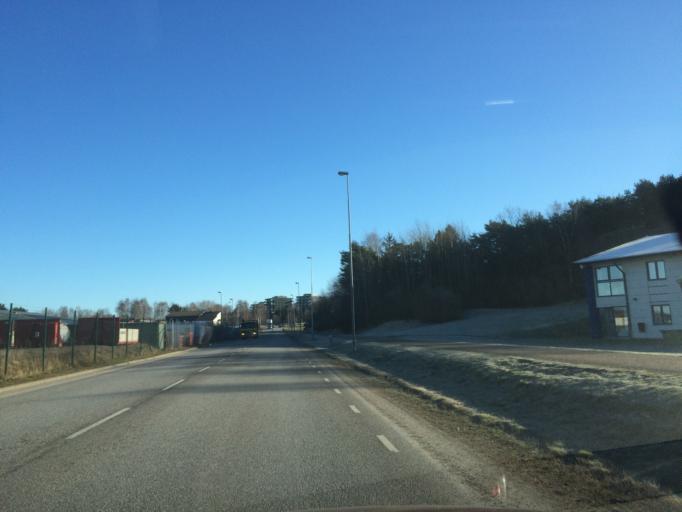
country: SE
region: Halland
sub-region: Kungsbacka Kommun
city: Kungsbacka
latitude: 57.4779
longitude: 12.0838
